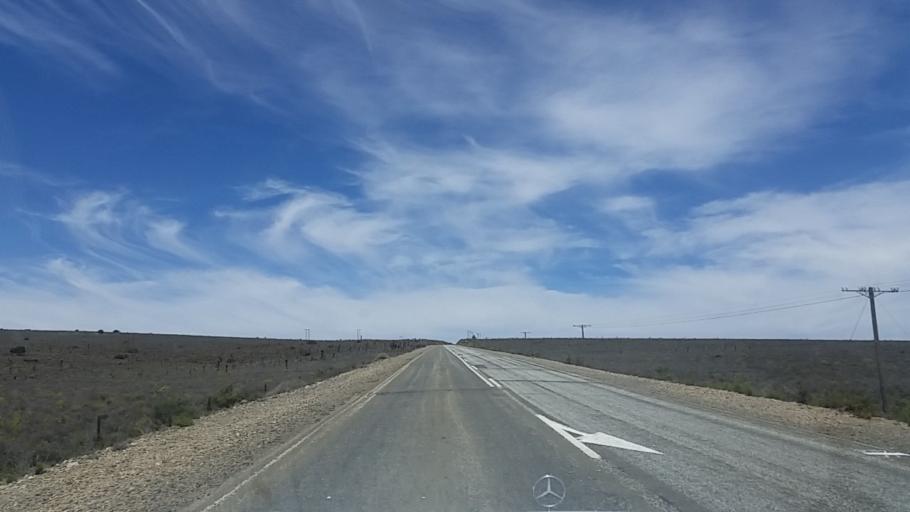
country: ZA
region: Eastern Cape
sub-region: Cacadu District Municipality
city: Willowmore
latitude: -33.5770
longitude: 23.1675
